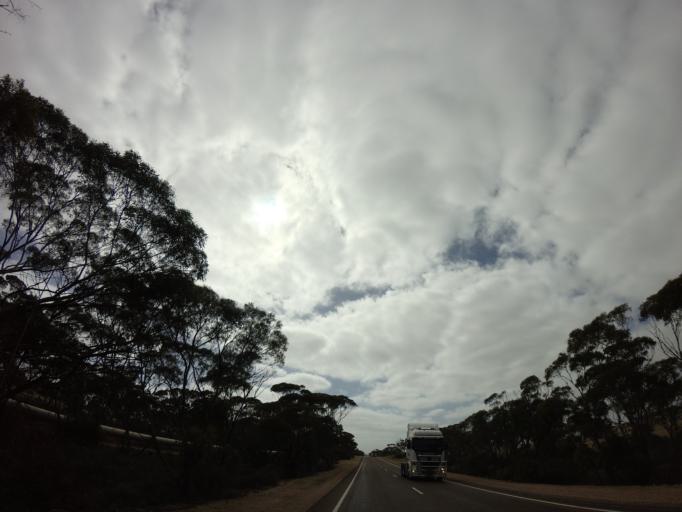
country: AU
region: South Australia
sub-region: Streaky Bay
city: Streaky Bay
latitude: -32.7276
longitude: 134.8691
